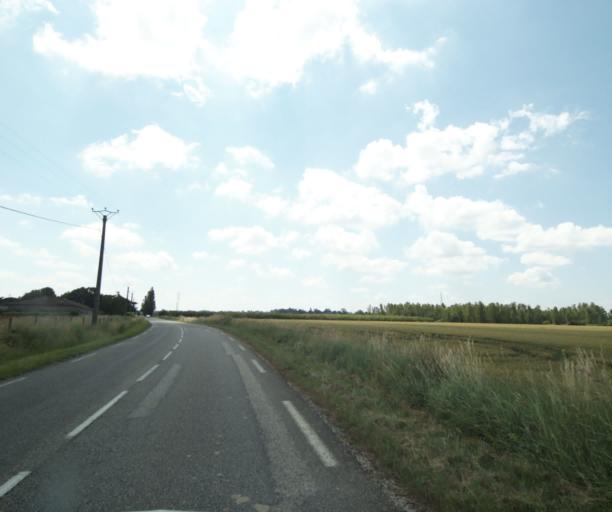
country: FR
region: Midi-Pyrenees
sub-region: Departement du Tarn-et-Garonne
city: Montauban
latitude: 44.0684
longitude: 1.3532
